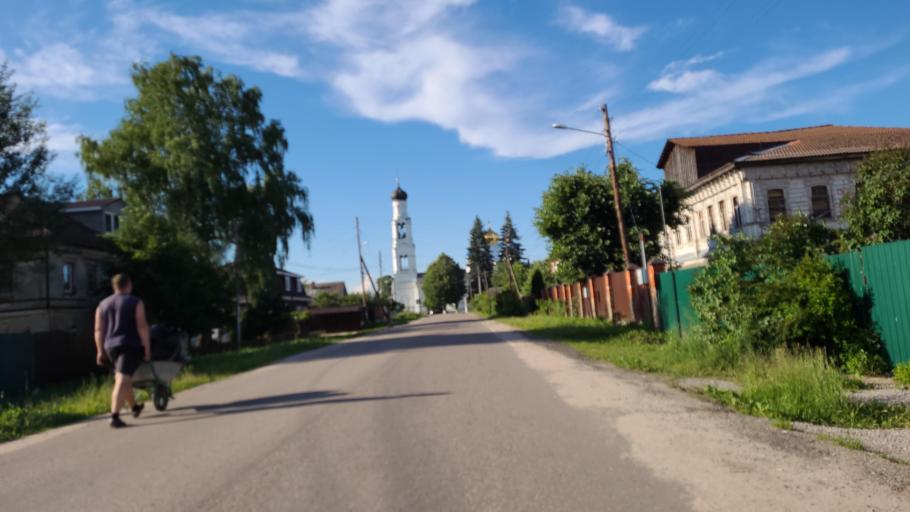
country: RU
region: Moskovskaya
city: Ashitkovo
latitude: 55.4372
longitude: 38.6047
